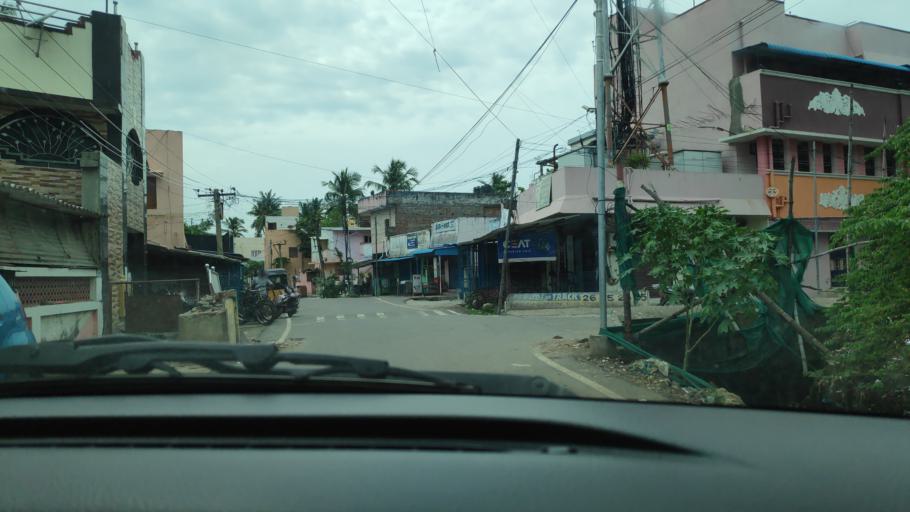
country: IN
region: Tamil Nadu
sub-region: Kancheepuram
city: Pallavaram
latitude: 12.9328
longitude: 80.1336
